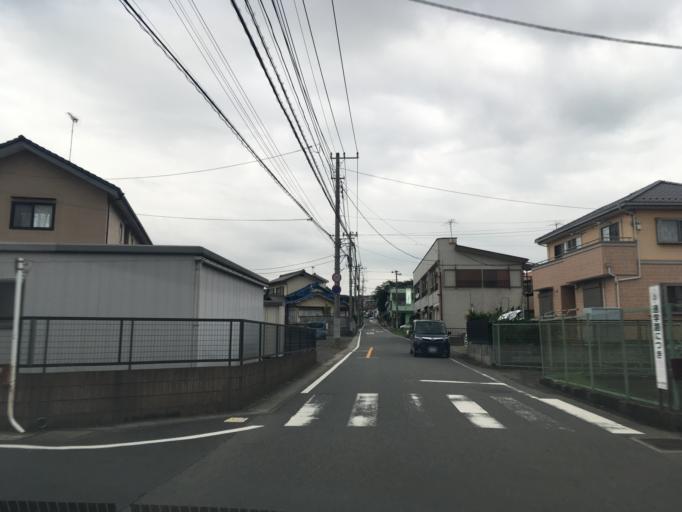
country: JP
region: Saitama
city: Sayama
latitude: 35.8299
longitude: 139.3695
